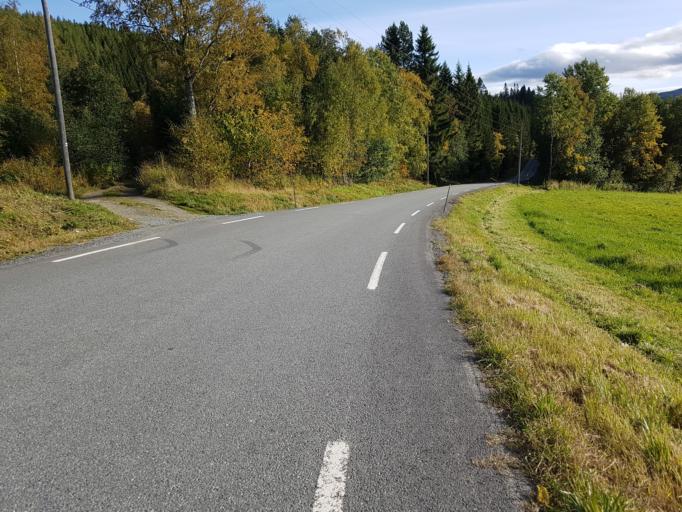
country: NO
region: Sor-Trondelag
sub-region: Malvik
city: Malvik
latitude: 63.3636
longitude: 10.6262
